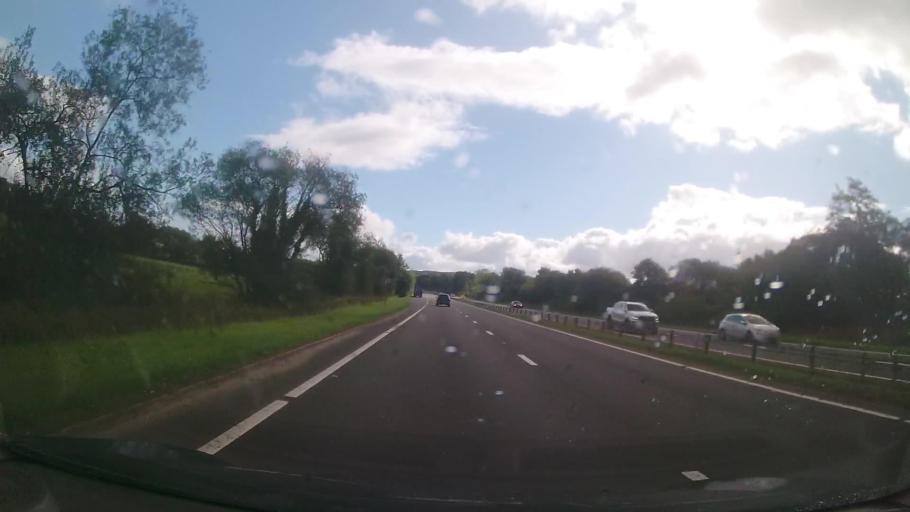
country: GB
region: Wales
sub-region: Carmarthenshire
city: Carmarthen
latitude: 51.8402
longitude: -4.2895
